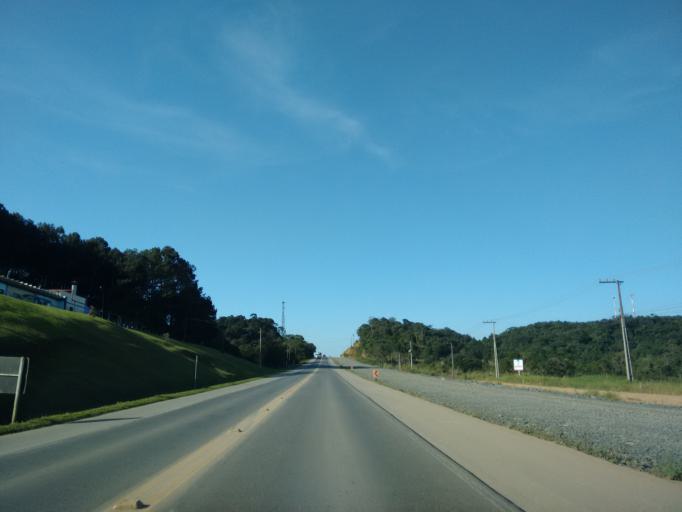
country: BR
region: Santa Catarina
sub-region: Guaramirim
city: Guaramirim
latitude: -26.4597
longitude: -48.9399
